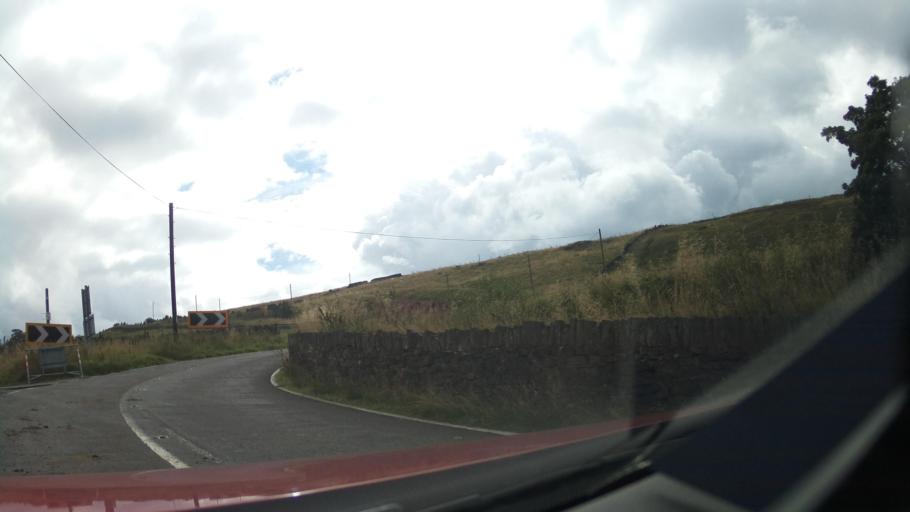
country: GB
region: England
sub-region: Kirklees
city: Meltham
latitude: 53.5446
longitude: -1.8473
